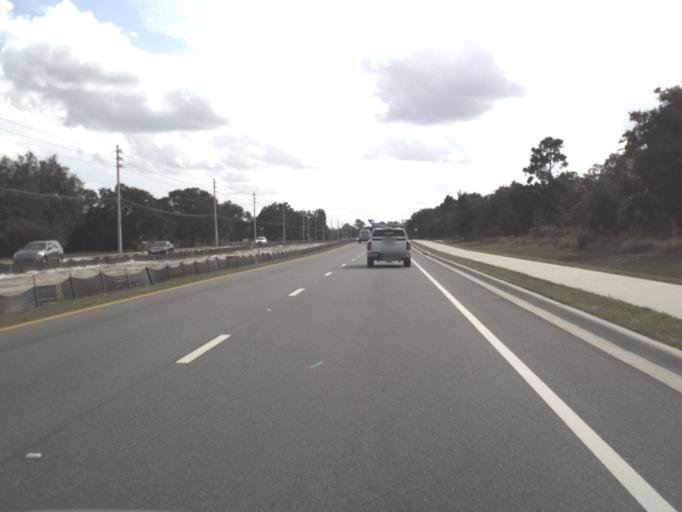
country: US
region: Florida
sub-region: Osceola County
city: Saint Cloud
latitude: 28.2865
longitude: -81.2441
